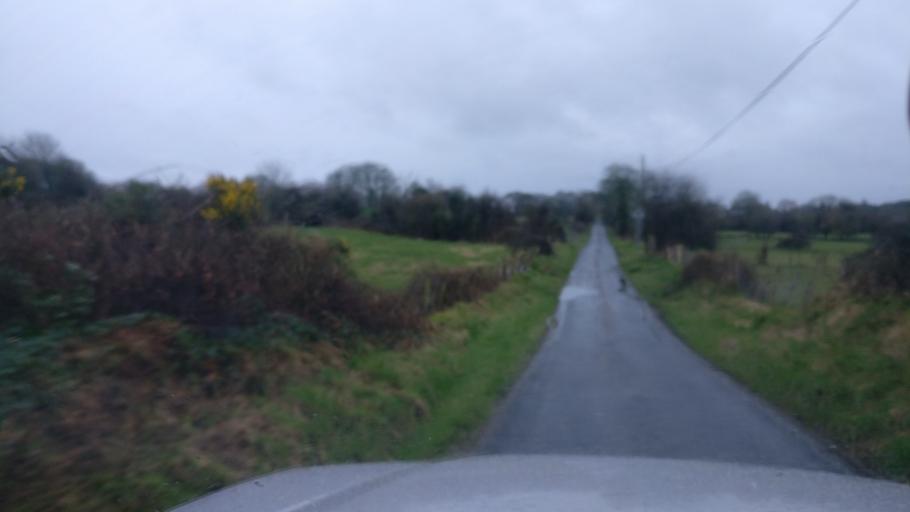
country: IE
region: Connaught
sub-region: County Galway
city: Ballinasloe
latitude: 53.2886
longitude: -8.2865
